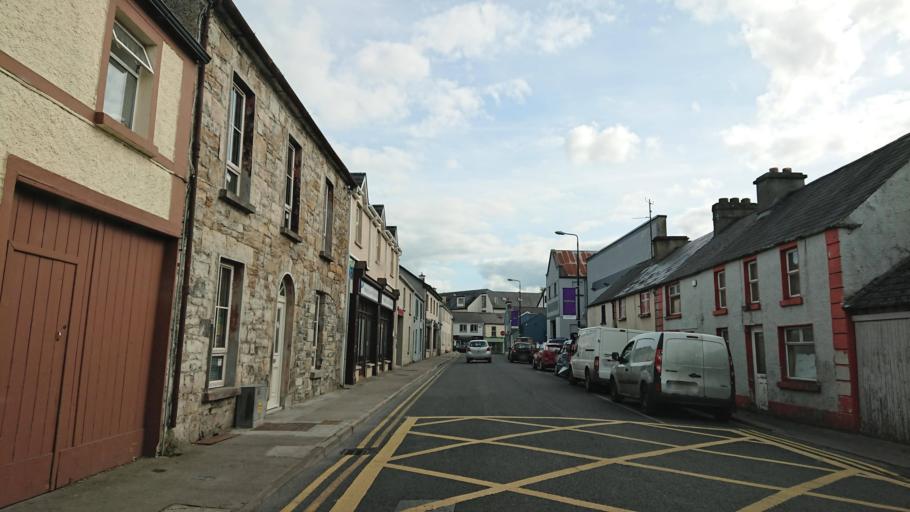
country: IE
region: Connaught
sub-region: County Leitrim
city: Carrick-on-Shannon
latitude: 53.9479
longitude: -8.0917
